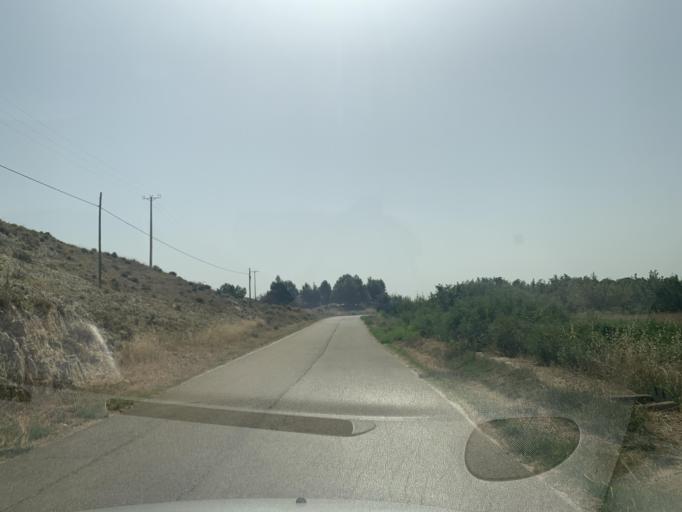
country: ES
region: Aragon
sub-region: Provincia de Zaragoza
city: Almonacid de la Cuba
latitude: 41.2740
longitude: -0.7863
